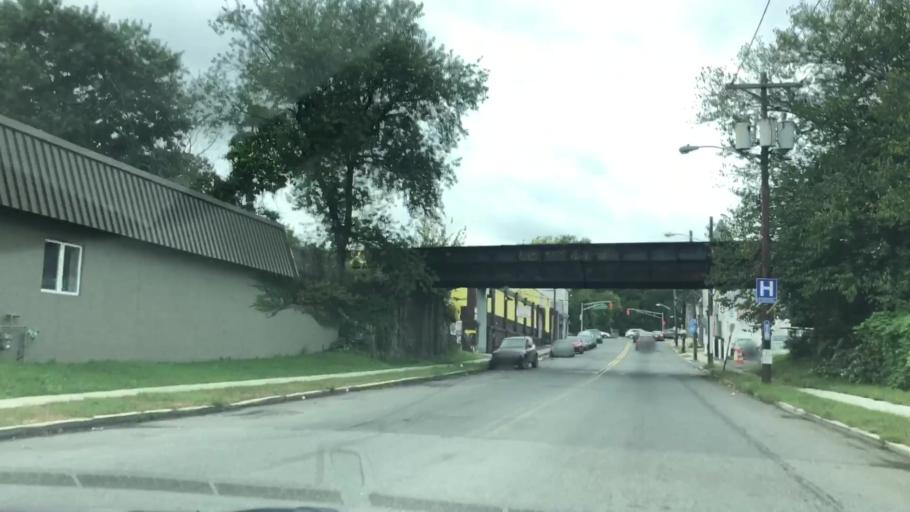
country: US
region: New Jersey
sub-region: Essex County
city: Belleville
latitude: 40.7812
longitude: -74.1527
